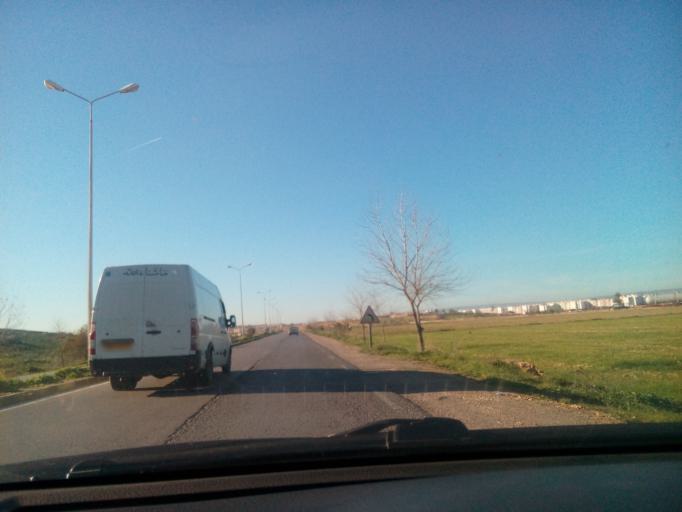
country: DZ
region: Relizane
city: Relizane
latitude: 35.7119
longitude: 0.5504
